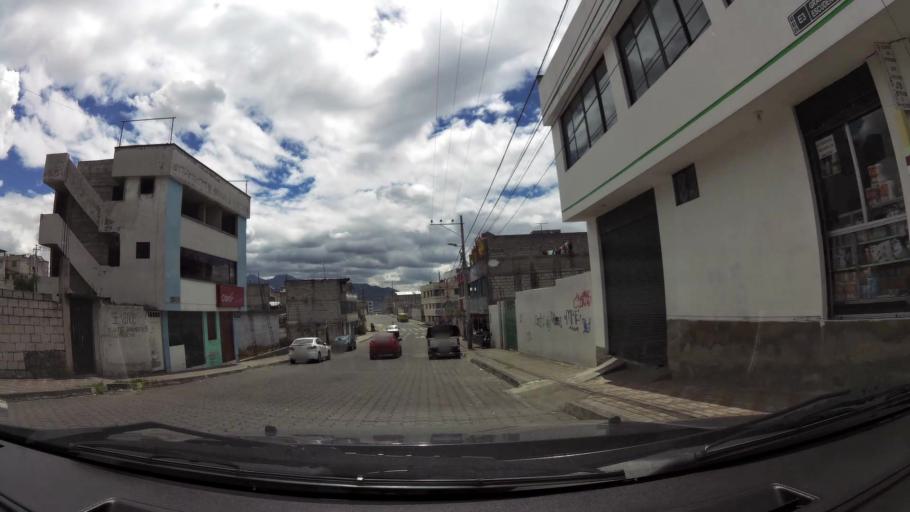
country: EC
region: Pichincha
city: Sangolqui
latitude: -0.3360
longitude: -78.5451
